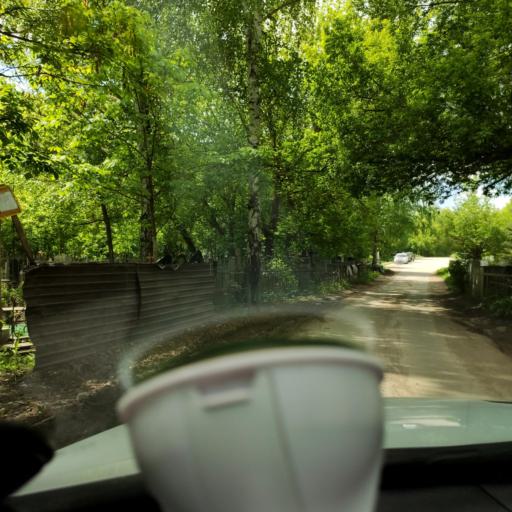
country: RU
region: Samara
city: Petra-Dubrava
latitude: 53.2747
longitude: 50.3221
